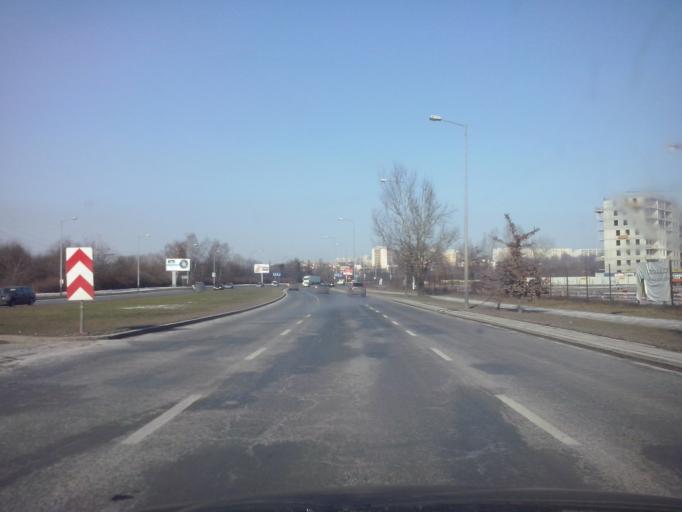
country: PL
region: Lesser Poland Voivodeship
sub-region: Krakow
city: Krakow
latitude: 50.0786
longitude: 20.0005
